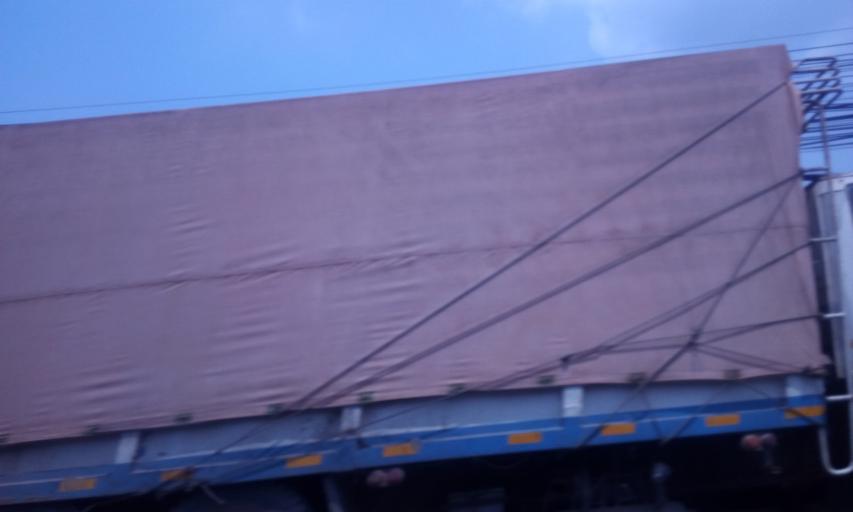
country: TH
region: Chachoengsao
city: Chachoengsao
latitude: 13.6700
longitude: 101.0861
